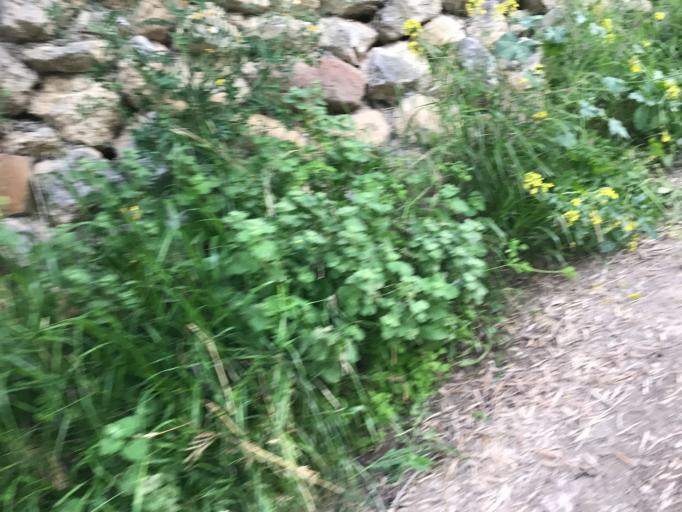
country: ES
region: Andalusia
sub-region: Provincia de Granada
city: Castril
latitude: 37.7920
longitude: -2.7799
